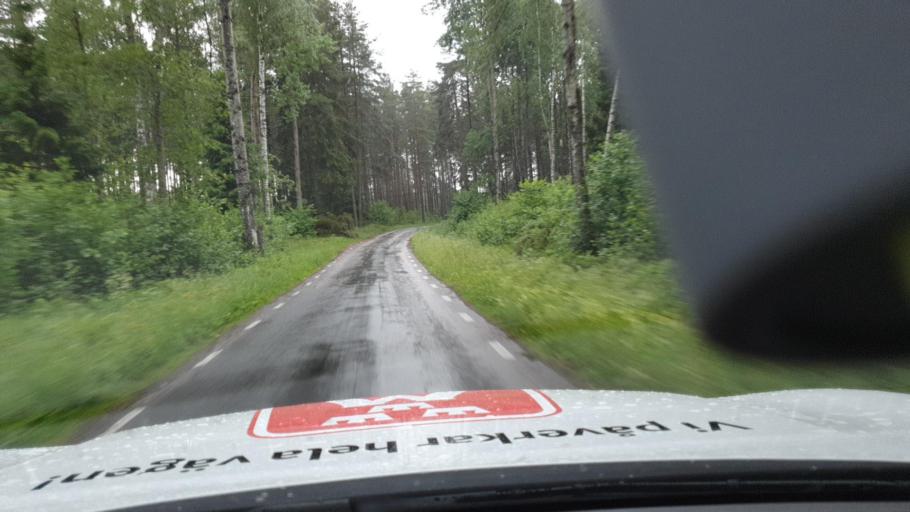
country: SE
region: Vaestra Goetaland
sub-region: Skovde Kommun
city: Stopen
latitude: 58.4647
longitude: 13.9177
